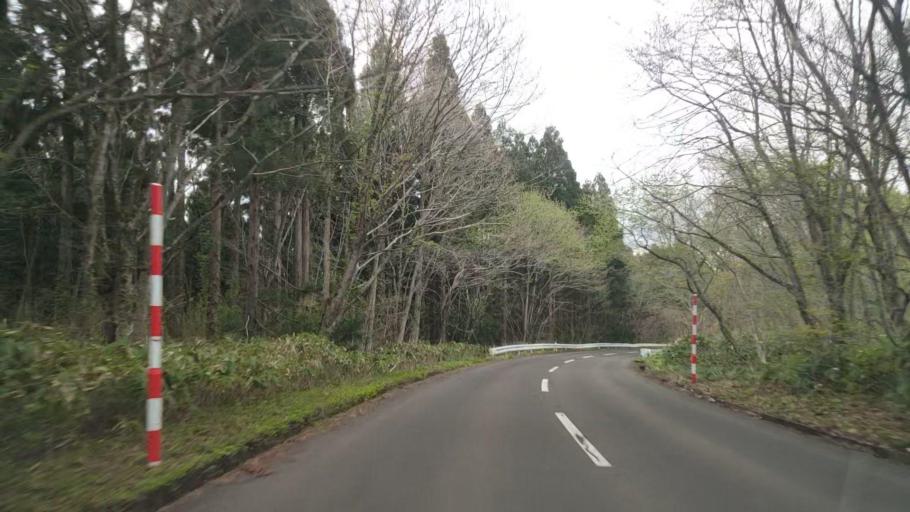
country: JP
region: Akita
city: Hanawa
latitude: 40.3907
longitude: 140.7950
